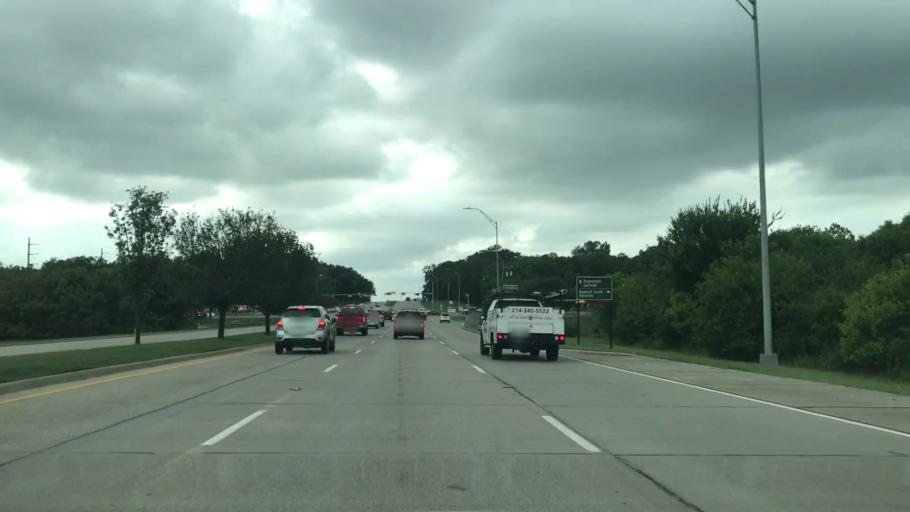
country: US
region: Texas
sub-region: Dallas County
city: Rowlett
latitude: 32.9100
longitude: -96.5962
